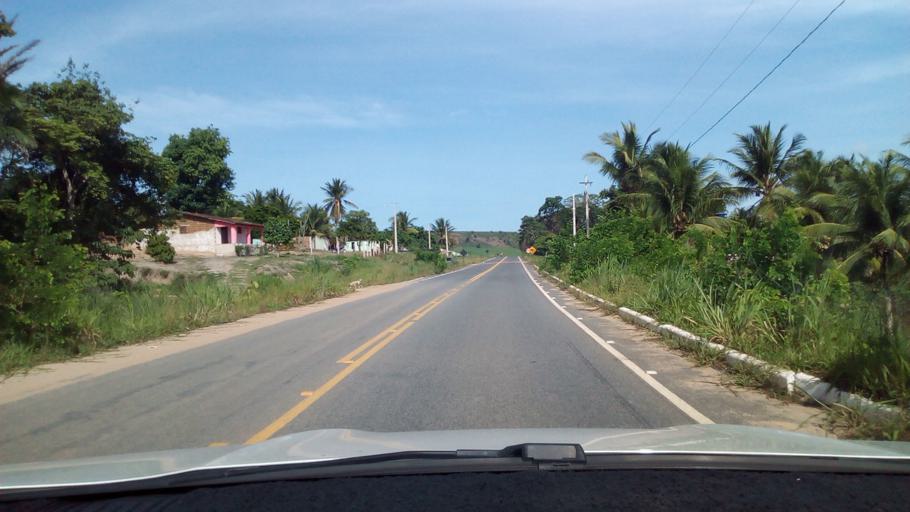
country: BR
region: Paraiba
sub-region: Santa Rita
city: Santa Rita
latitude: -7.0596
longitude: -34.9420
